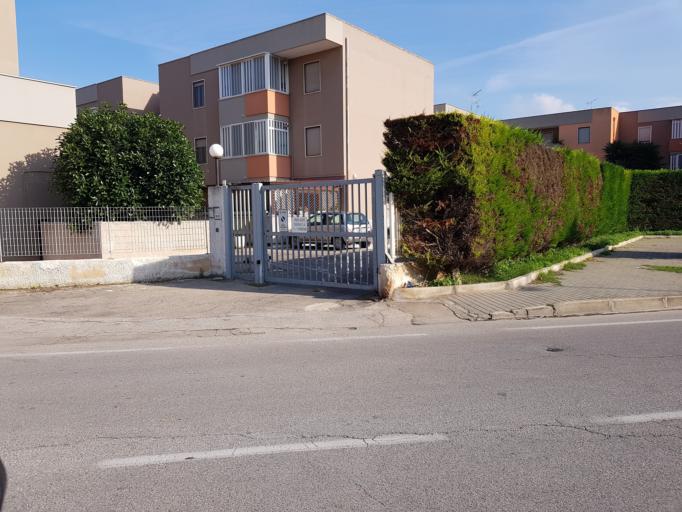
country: IT
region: Apulia
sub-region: Provincia di Brindisi
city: Materdomini
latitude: 40.6584
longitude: 17.9578
